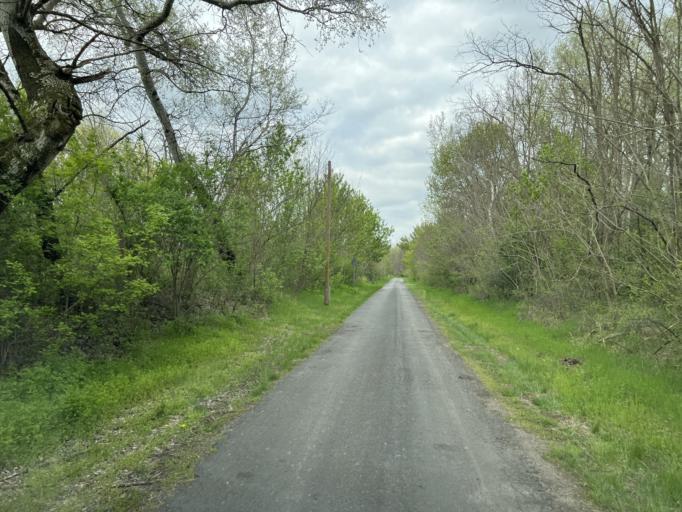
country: HU
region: Pest
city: Orkeny
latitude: 47.0438
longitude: 19.3516
